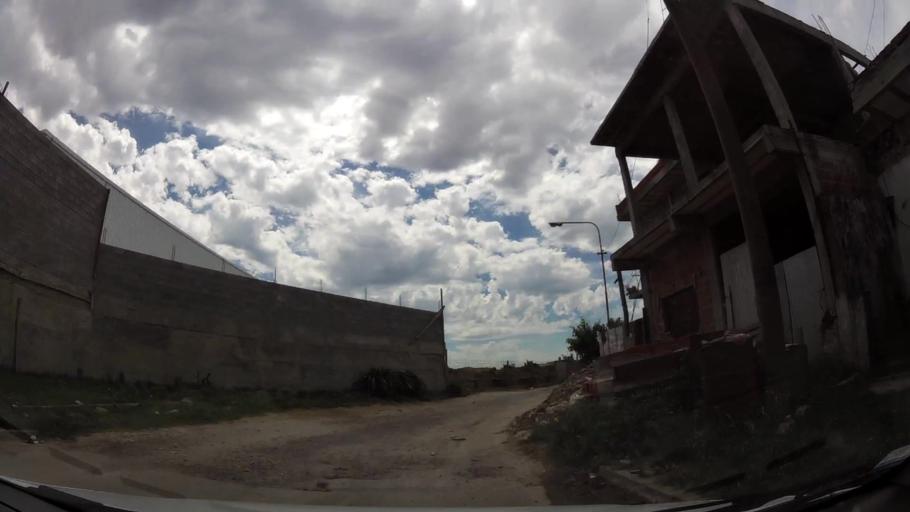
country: AR
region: Buenos Aires
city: San Justo
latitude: -34.6887
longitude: -58.5439
